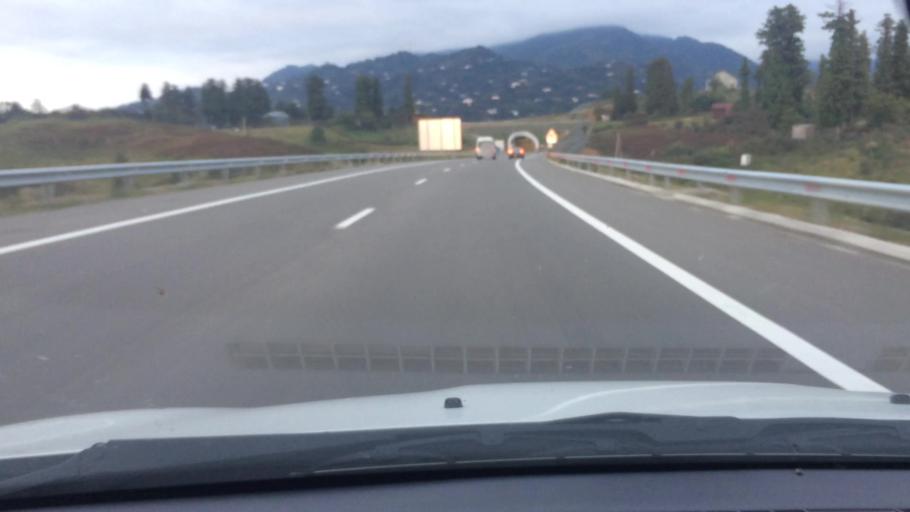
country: GE
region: Ajaria
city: Makhinjauri
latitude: 41.7075
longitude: 41.7429
